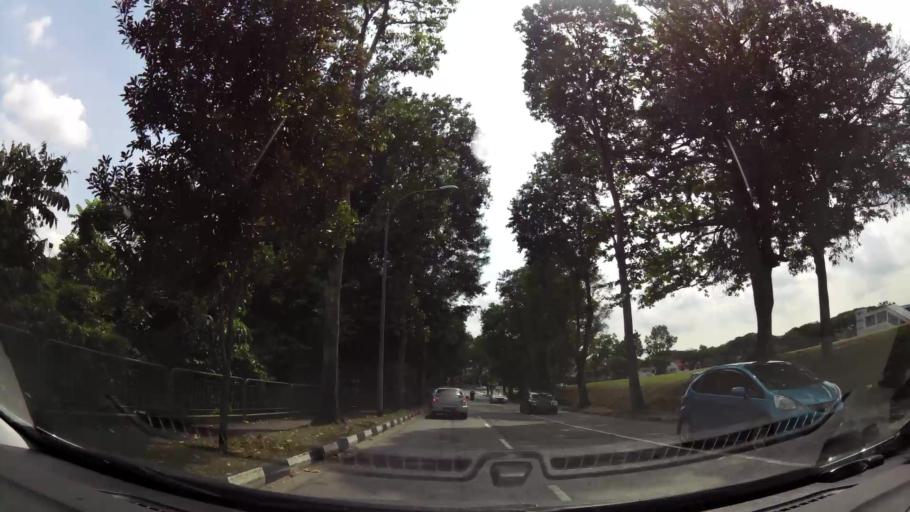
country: SG
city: Singapore
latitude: 1.3328
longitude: 103.7968
